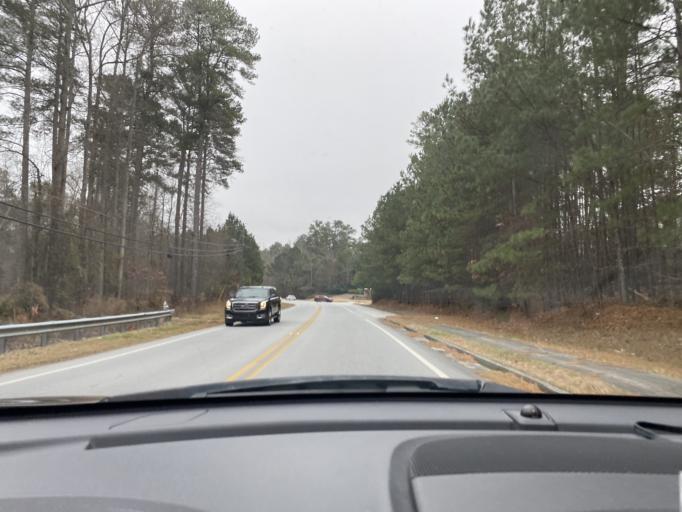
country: US
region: Georgia
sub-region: Gwinnett County
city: Grayson
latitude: 33.9103
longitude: -83.9309
